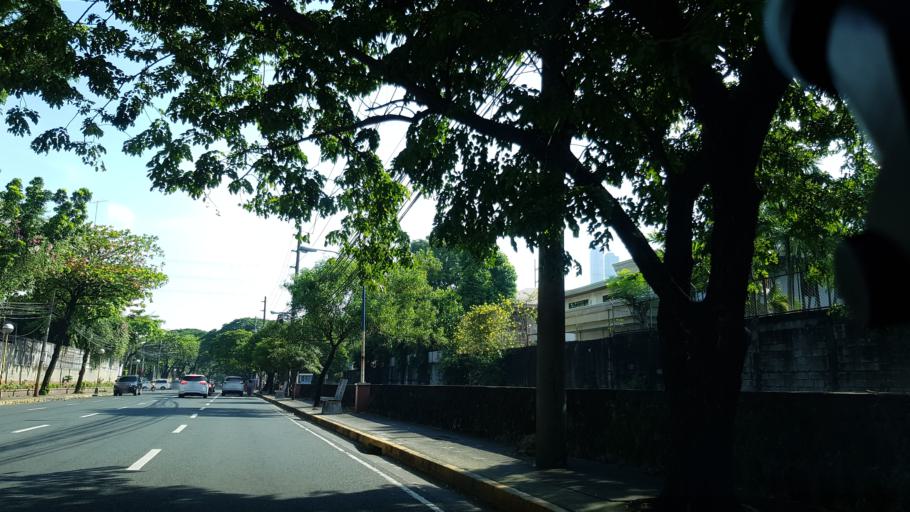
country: PH
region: Metro Manila
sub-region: Pasig
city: Pasig City
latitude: 14.5854
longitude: 121.0710
